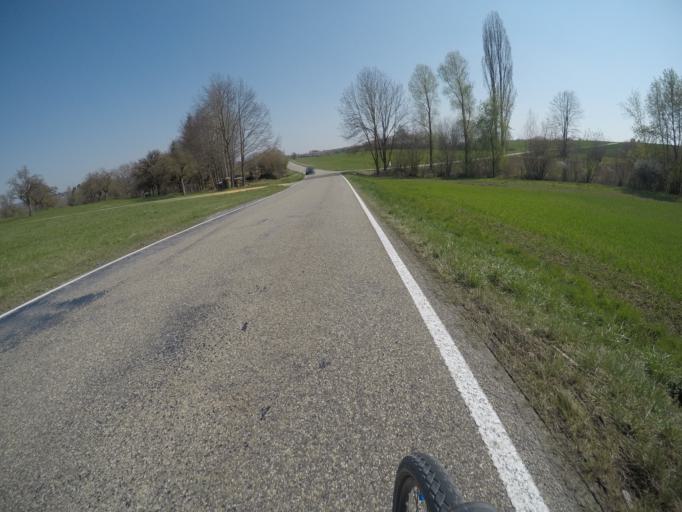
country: DE
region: Baden-Wuerttemberg
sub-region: Regierungsbezirk Stuttgart
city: Renningen
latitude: 48.7446
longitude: 8.9332
